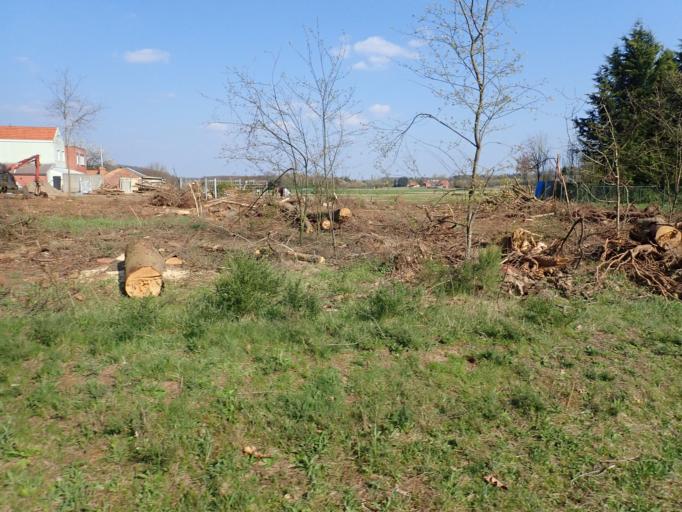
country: BE
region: Flanders
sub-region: Provincie Vlaams-Brabant
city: Aarschot
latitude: 50.9590
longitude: 4.8149
